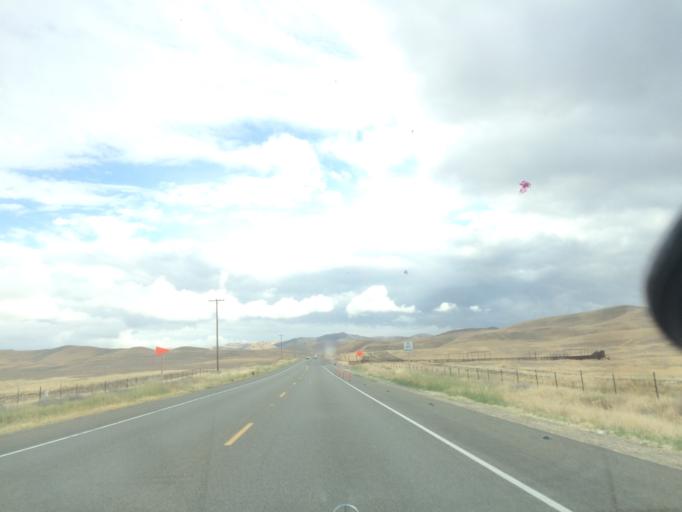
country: US
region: California
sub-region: San Luis Obispo County
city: Shandon
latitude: 35.7421
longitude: -120.2765
